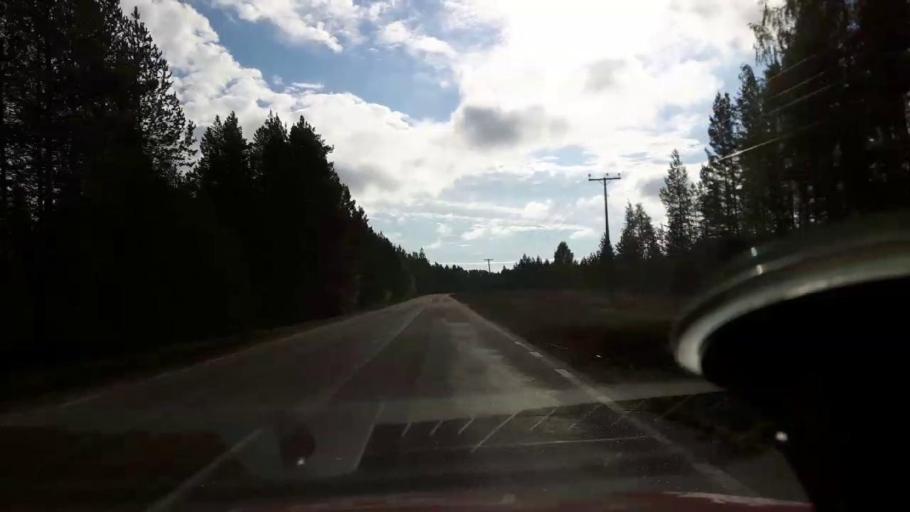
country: SE
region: Jaemtland
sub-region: Harjedalens Kommun
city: Sveg
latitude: 62.1146
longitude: 15.0502
